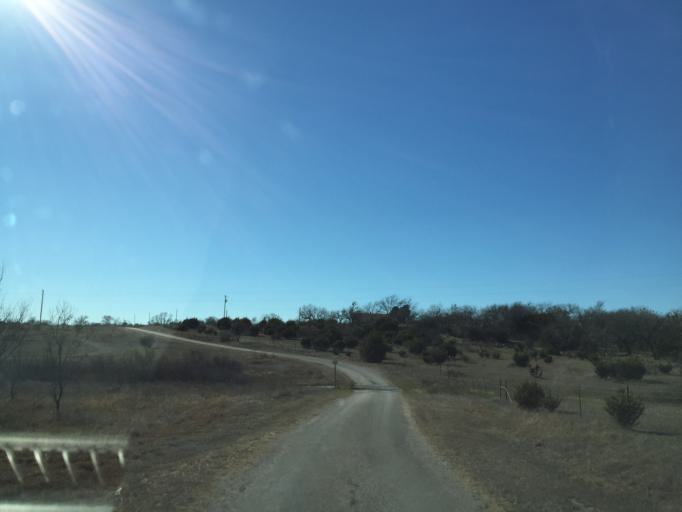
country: US
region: Texas
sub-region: Lampasas County
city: Lampasas
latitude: 30.9375
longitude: -98.1714
